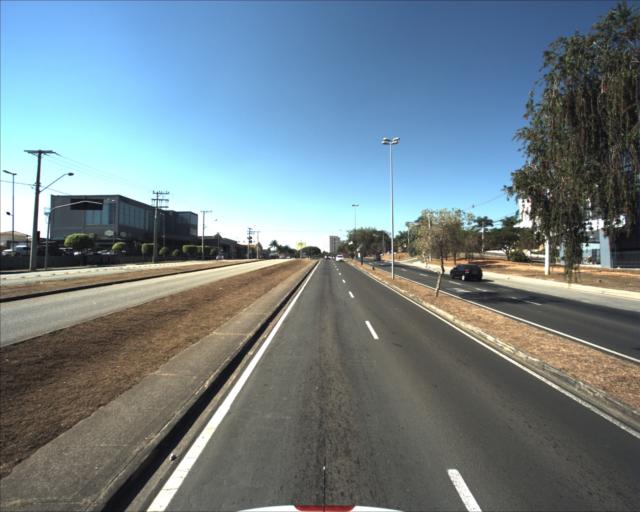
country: BR
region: Sao Paulo
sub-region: Sorocaba
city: Sorocaba
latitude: -23.4918
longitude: -47.4127
